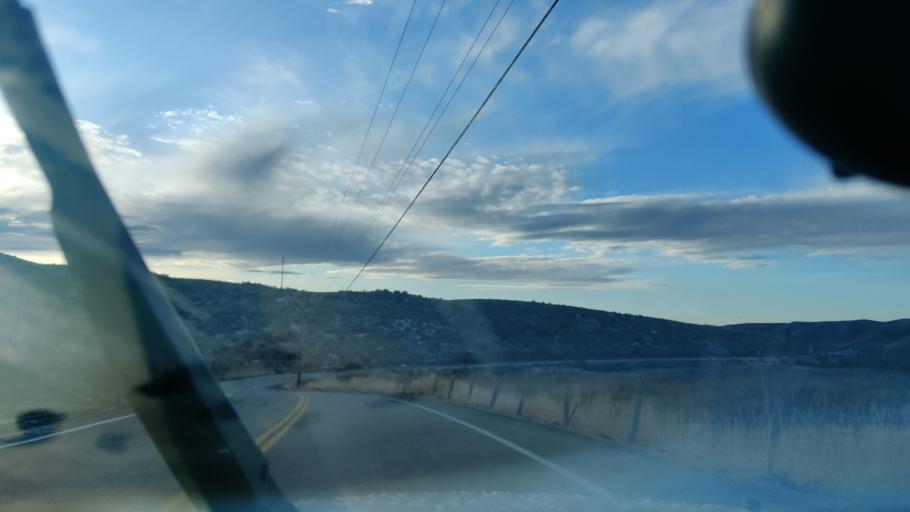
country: US
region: Idaho
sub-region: Ada County
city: Eagle
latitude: 43.7293
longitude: -116.2808
